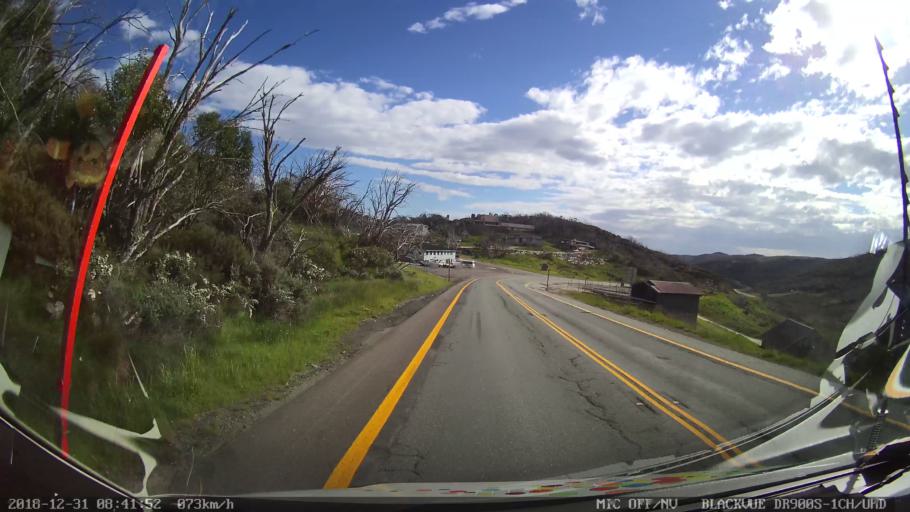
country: AU
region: New South Wales
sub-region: Snowy River
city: Jindabyne
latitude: -36.3953
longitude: 148.4262
